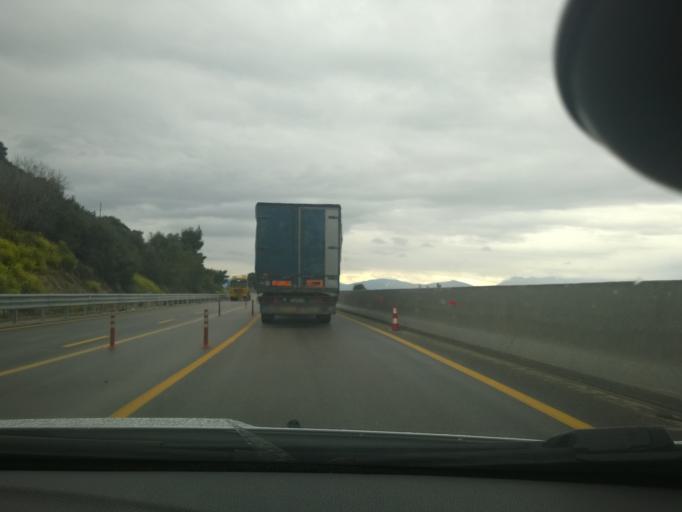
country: GR
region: West Greece
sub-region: Nomos Achaias
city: Siliveniotika
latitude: 38.1622
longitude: 22.3363
